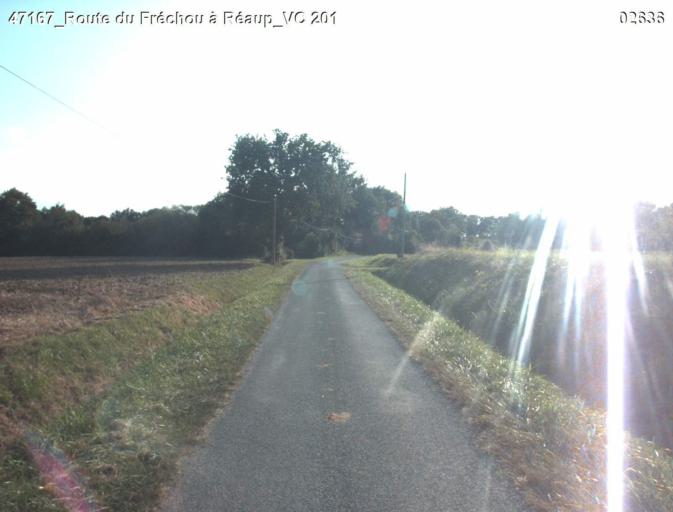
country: FR
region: Aquitaine
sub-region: Departement du Lot-et-Garonne
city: Mezin
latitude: 44.0726
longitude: 0.2833
